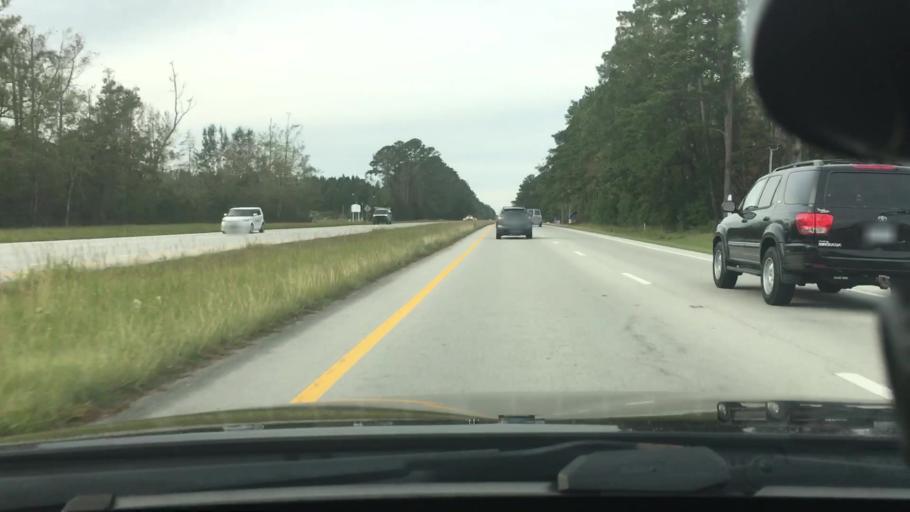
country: US
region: North Carolina
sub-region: Craven County
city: Fairfield Harbour
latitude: 35.0145
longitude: -76.9943
